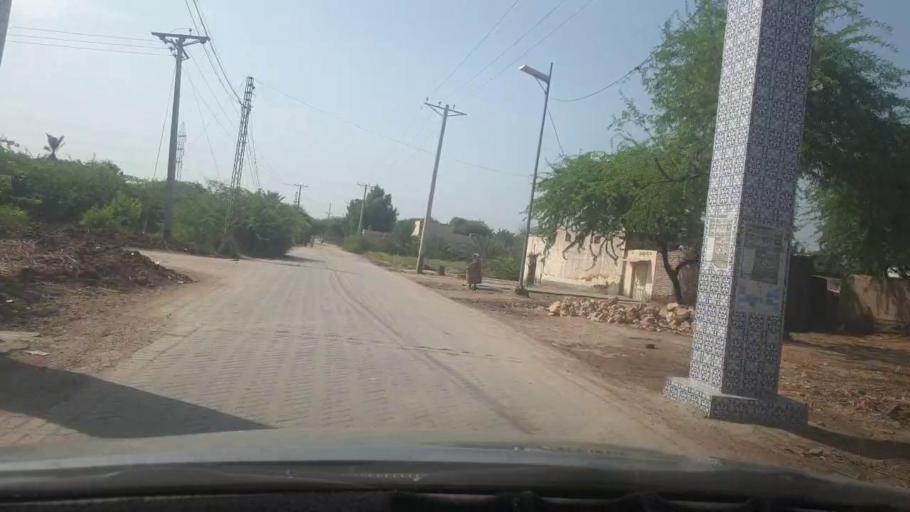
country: PK
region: Sindh
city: Gambat
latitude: 27.3338
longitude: 68.5471
